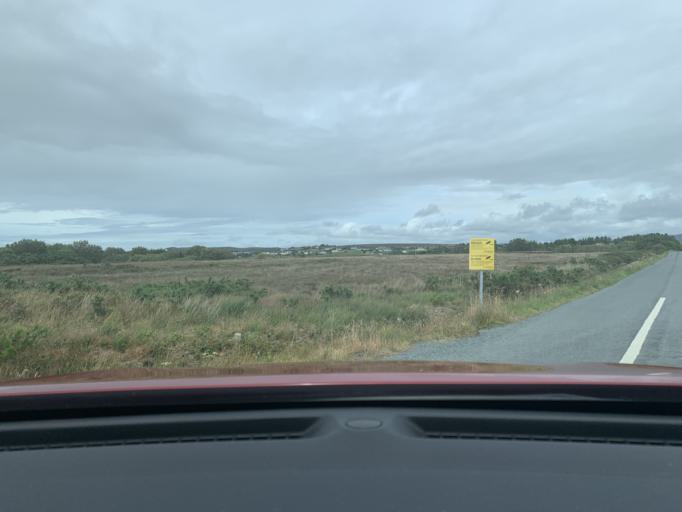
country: IE
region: Ulster
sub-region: County Donegal
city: Dungloe
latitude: 54.9587
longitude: -8.3726
